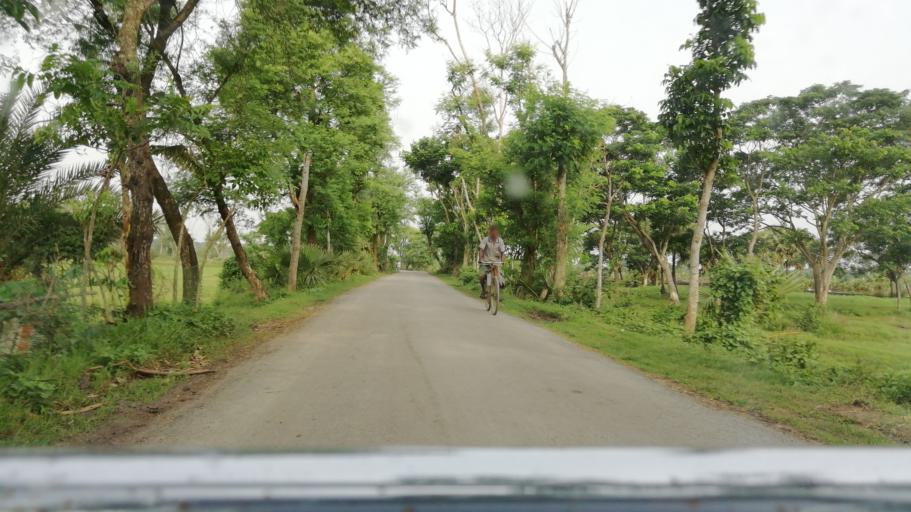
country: BD
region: Khulna
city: Bhatpara Abhaynagar
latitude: 23.0397
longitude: 89.3075
